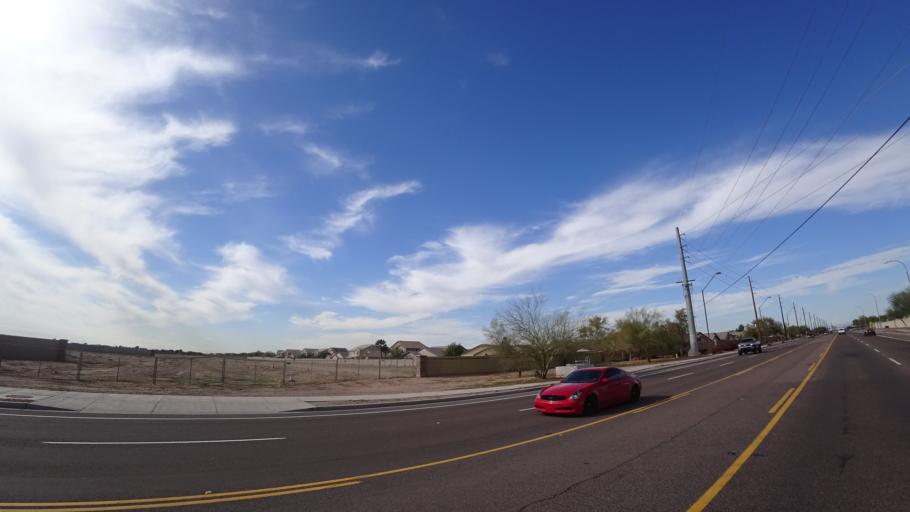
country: US
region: Arizona
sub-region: Maricopa County
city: Tolleson
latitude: 33.4426
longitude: -112.2899
